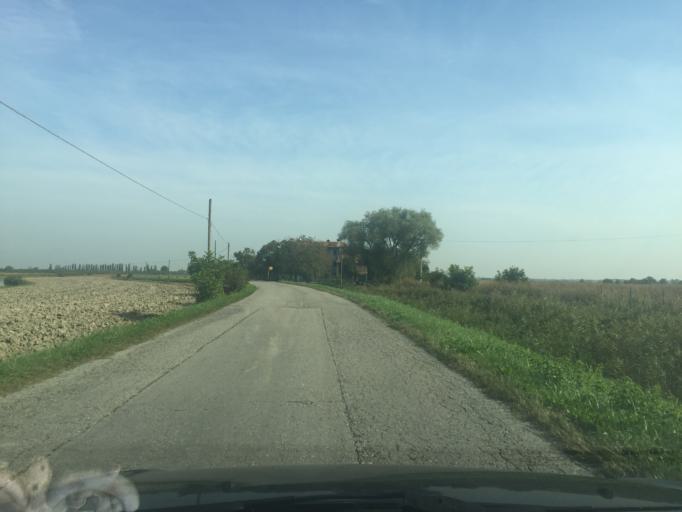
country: IT
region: Veneto
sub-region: Provincia di Venezia
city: Passarella
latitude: 45.6205
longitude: 12.6439
